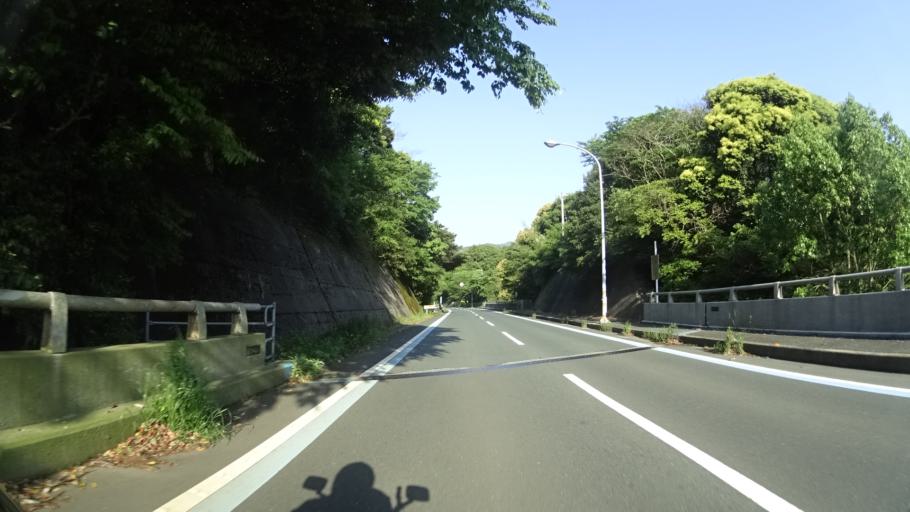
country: JP
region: Ehime
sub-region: Nishiuwa-gun
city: Ikata-cho
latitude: 33.3965
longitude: 132.1462
